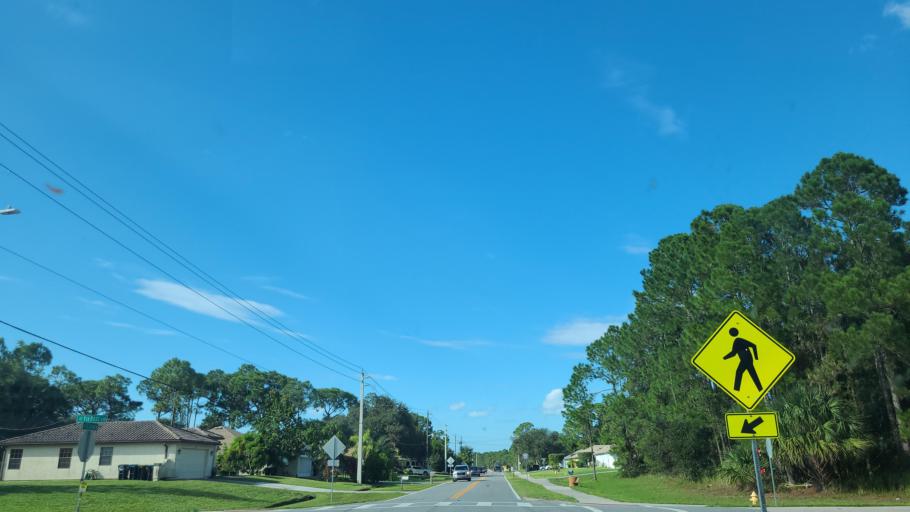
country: US
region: Florida
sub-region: Brevard County
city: Grant-Valkaria
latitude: 27.9674
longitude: -80.6609
